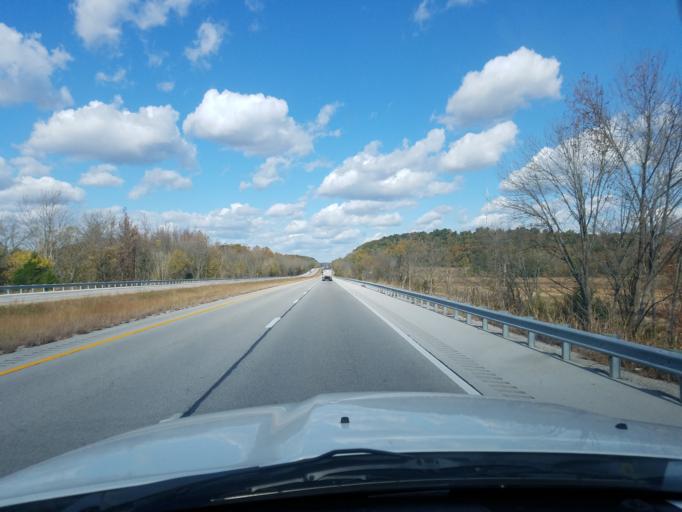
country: US
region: Kentucky
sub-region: Butler County
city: Morgantown
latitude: 37.1368
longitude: -86.6496
